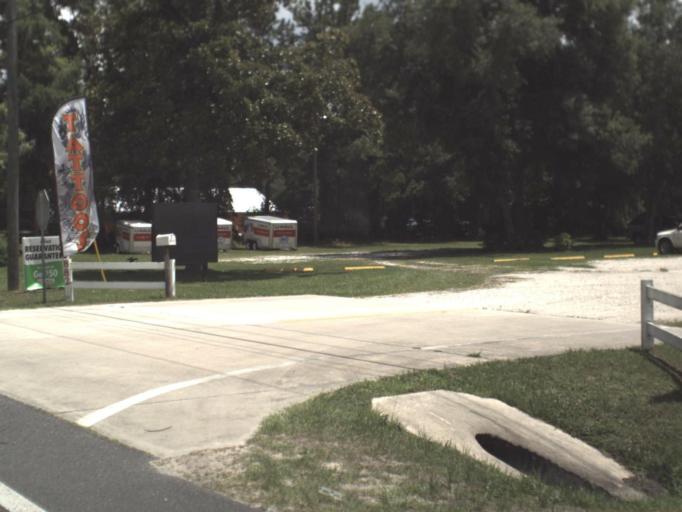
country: US
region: Florida
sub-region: Clay County
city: Keystone Heights
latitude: 29.7161
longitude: -82.0447
